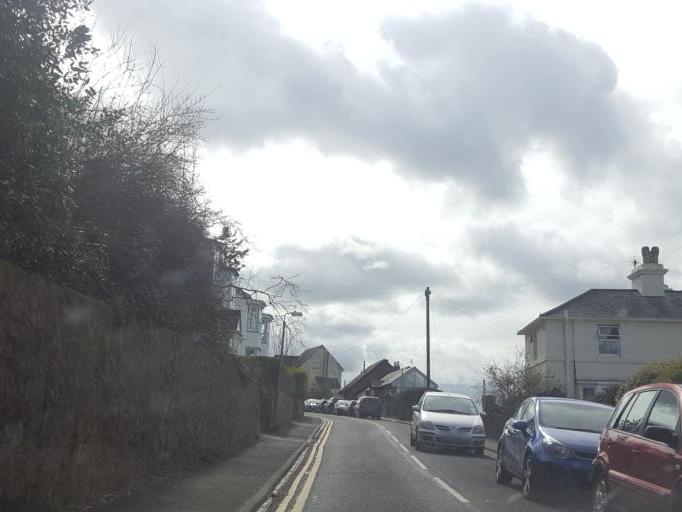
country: GB
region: England
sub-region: Worcestershire
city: Great Malvern
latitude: 52.1167
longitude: -2.3467
